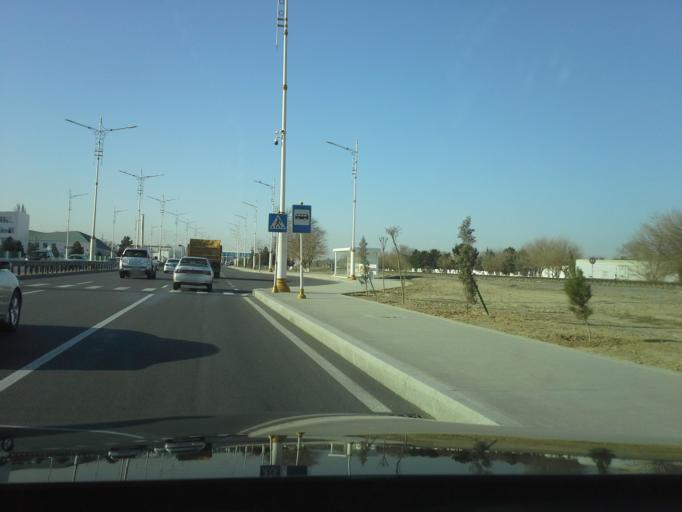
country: TM
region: Ahal
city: Ashgabat
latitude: 37.9567
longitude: 58.3705
